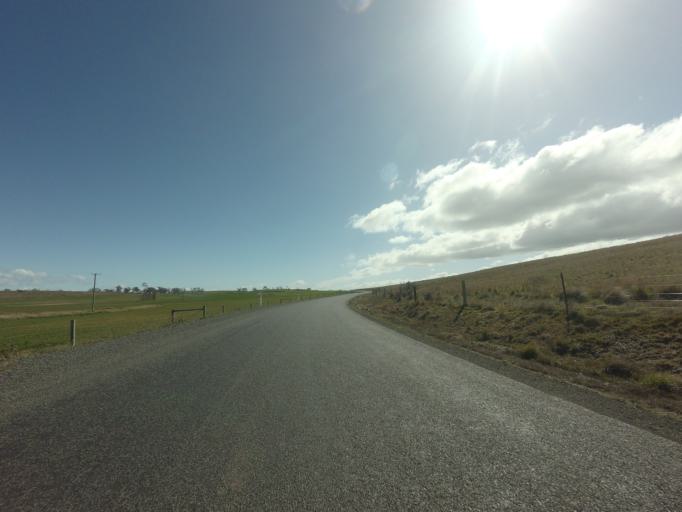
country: AU
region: Tasmania
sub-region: Northern Midlands
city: Evandale
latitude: -41.9164
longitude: 147.4730
